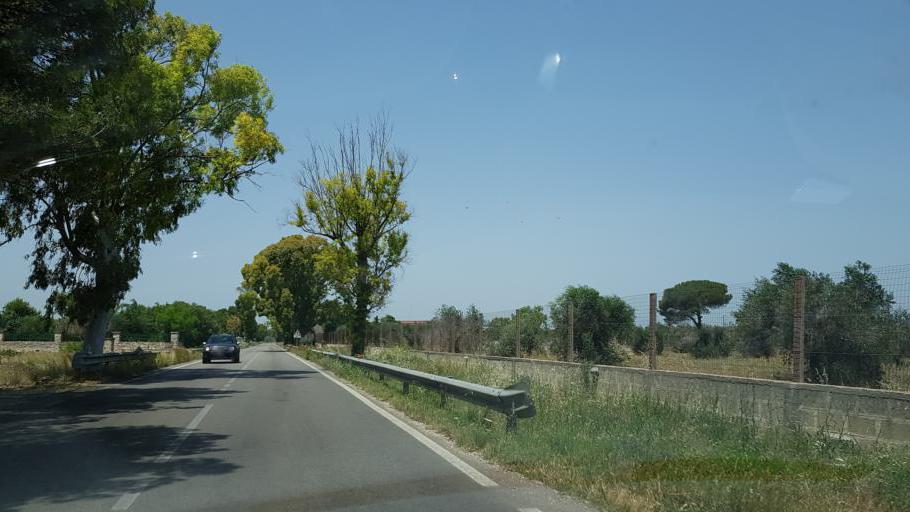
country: IT
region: Apulia
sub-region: Provincia di Lecce
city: Porto Cesareo
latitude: 40.2607
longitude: 17.9213
